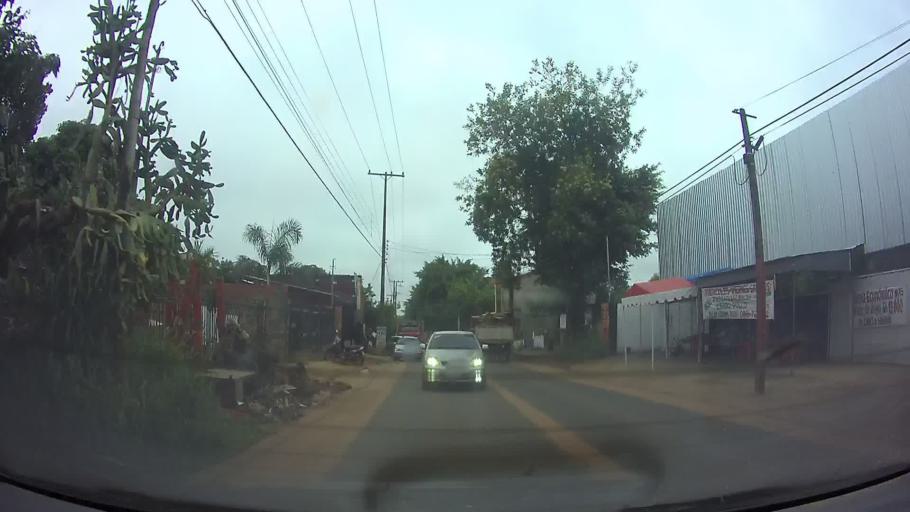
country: PY
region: Central
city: San Lorenzo
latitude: -25.3089
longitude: -57.4910
